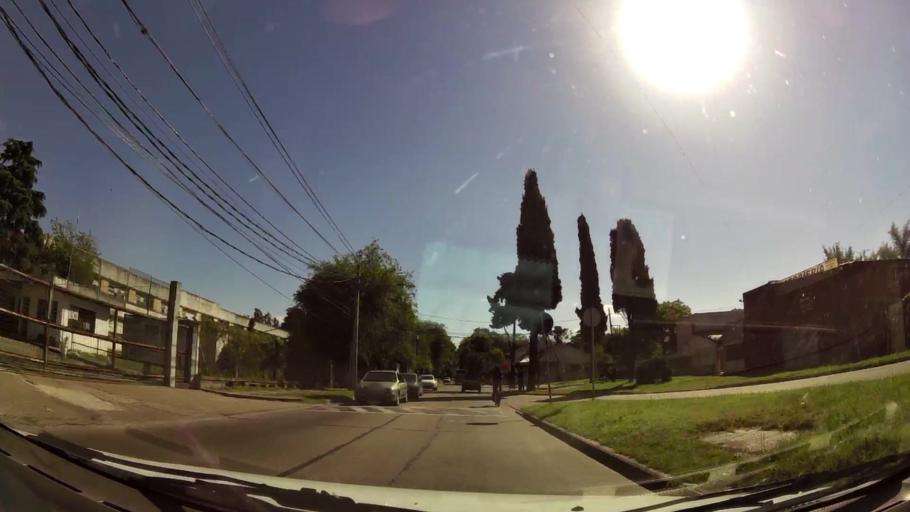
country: AR
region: Buenos Aires
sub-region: Partido de San Isidro
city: San Isidro
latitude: -34.4746
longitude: -58.5419
